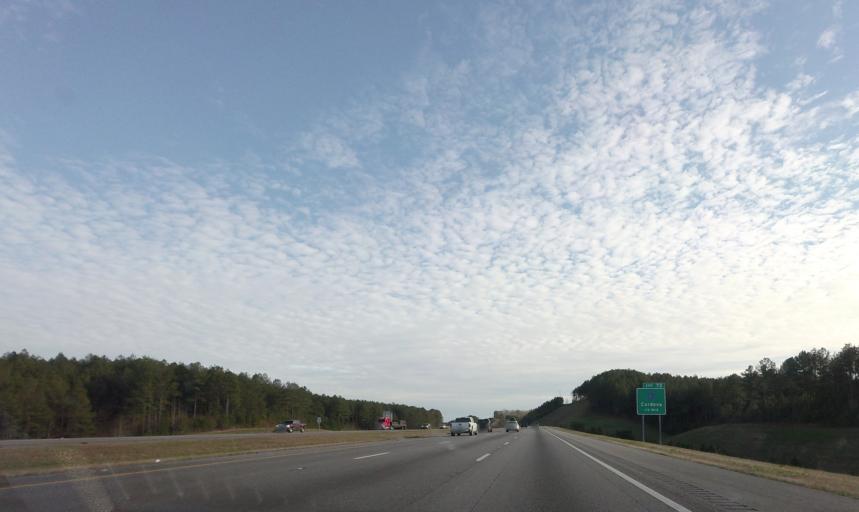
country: US
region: Alabama
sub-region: Walker County
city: Cordova
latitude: 33.7266
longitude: -87.1906
